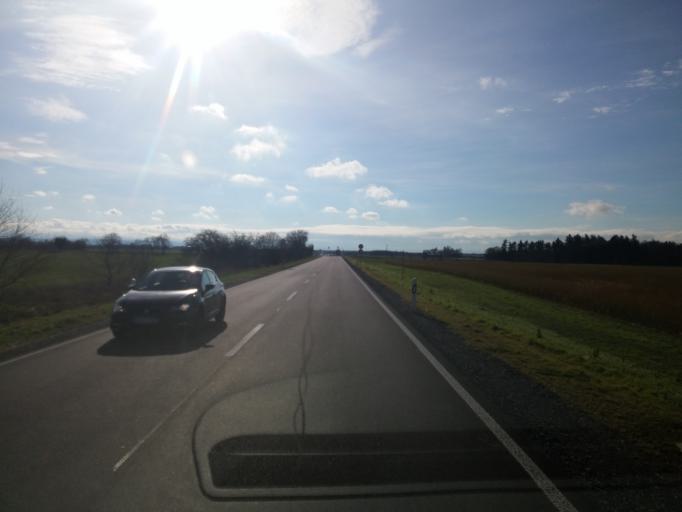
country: DE
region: Baden-Wuerttemberg
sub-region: Karlsruhe Region
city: Weingarten
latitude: 49.0920
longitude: 8.4842
